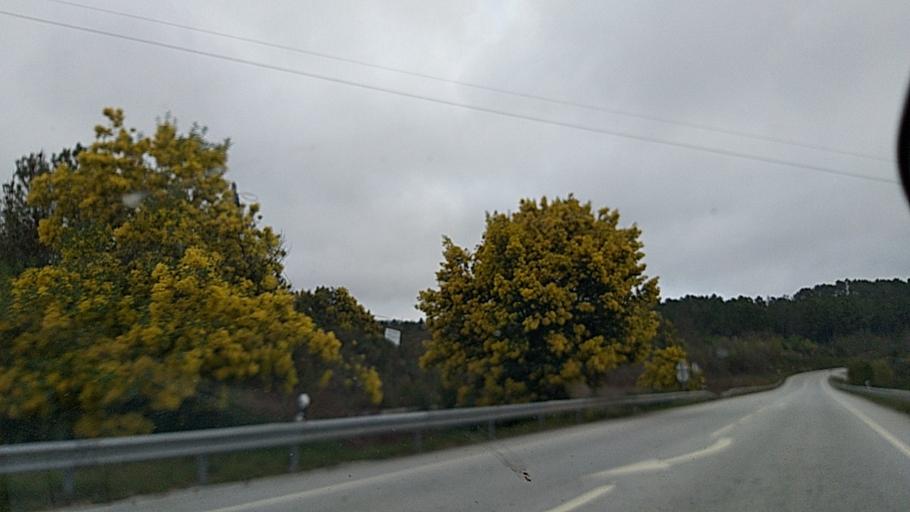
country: PT
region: Guarda
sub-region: Fornos de Algodres
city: Fornos de Algodres
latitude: 40.6188
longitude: -7.5118
